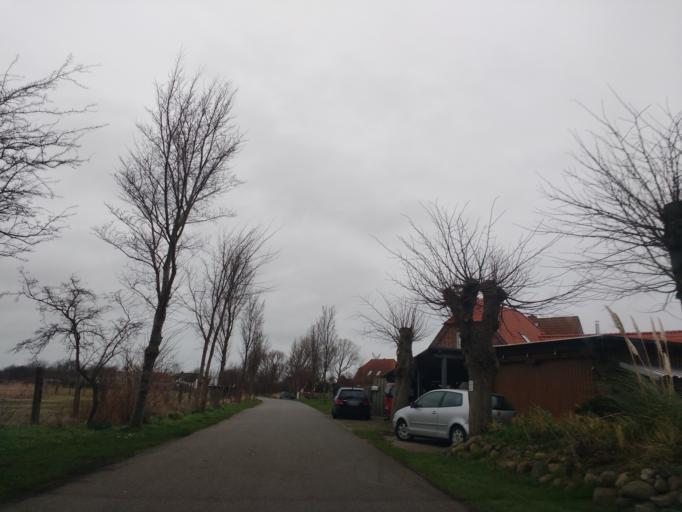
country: DE
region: Schleswig-Holstein
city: Grossenbrode
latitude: 54.3897
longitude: 11.1155
